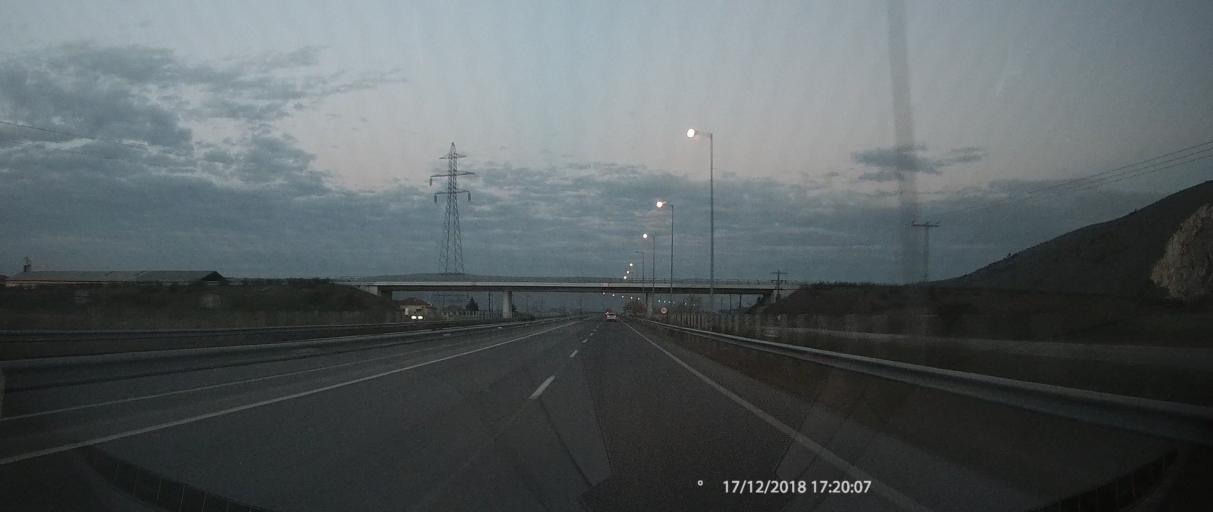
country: GR
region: Thessaly
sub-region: Trikala
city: Oichalia
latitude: 39.5779
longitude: 22.0108
